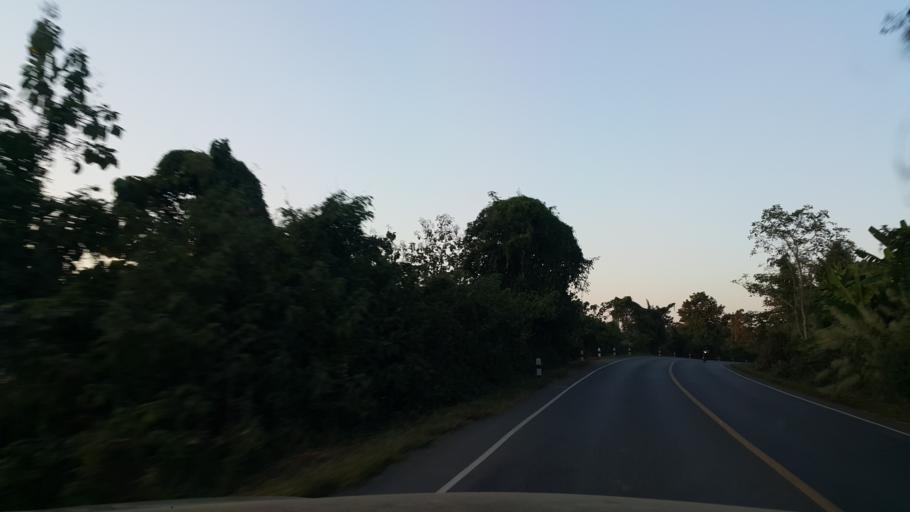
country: TH
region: Phrae
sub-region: Amphoe Wang Chin
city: Wang Chin
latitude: 17.8375
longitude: 99.6412
